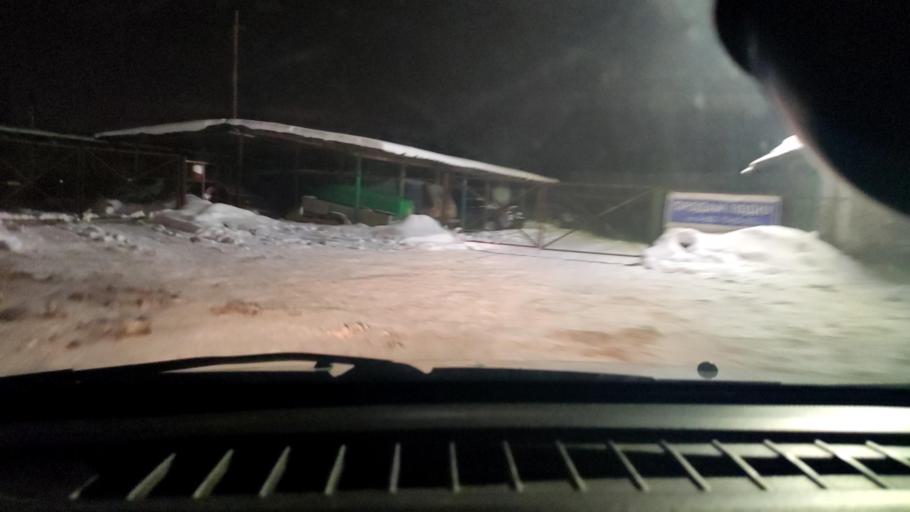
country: RU
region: Perm
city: Kondratovo
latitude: 58.0330
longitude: 56.0378
